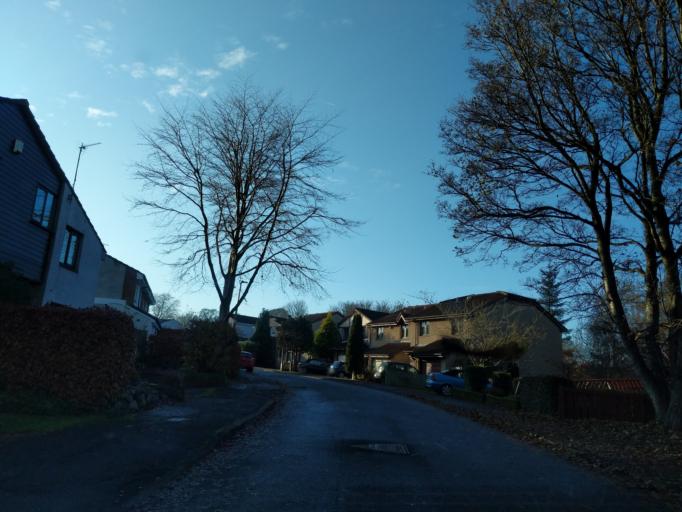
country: GB
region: Scotland
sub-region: Edinburgh
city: Colinton
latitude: 55.9056
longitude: -3.2674
